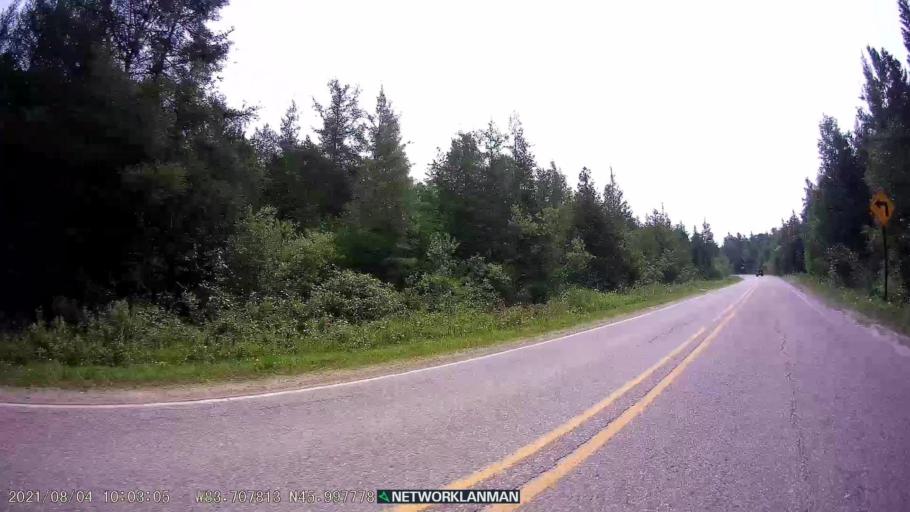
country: CA
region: Ontario
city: Thessalon
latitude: 45.9976
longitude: -83.7072
